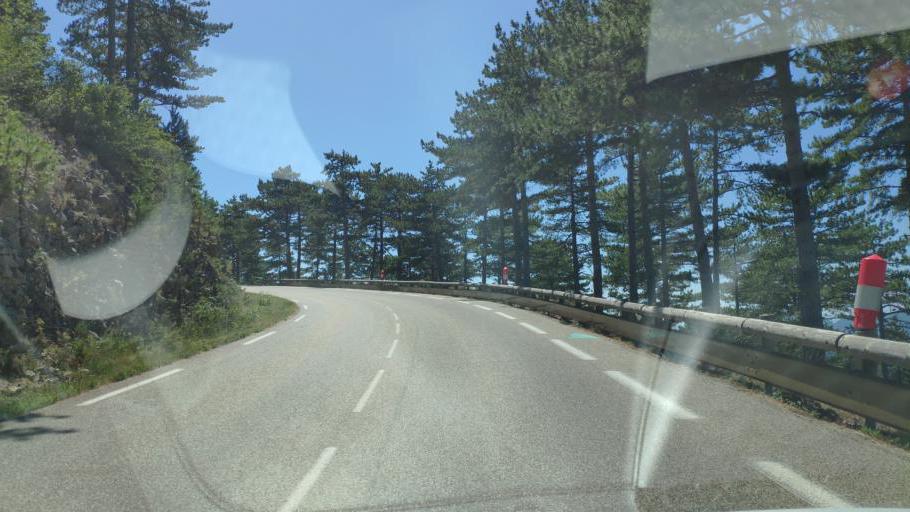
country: FR
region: Provence-Alpes-Cote d'Azur
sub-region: Departement du Vaucluse
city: Malaucene
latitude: 44.1591
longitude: 5.1484
